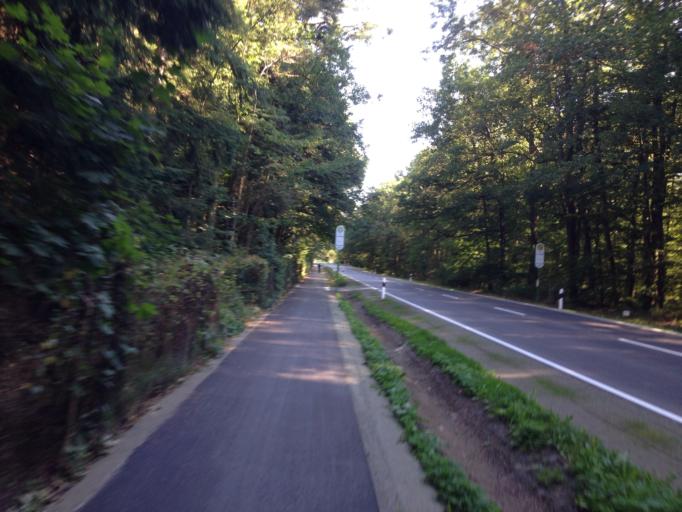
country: DE
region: Hesse
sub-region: Regierungsbezirk Giessen
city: Giessen
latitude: 50.5581
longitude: 8.7130
